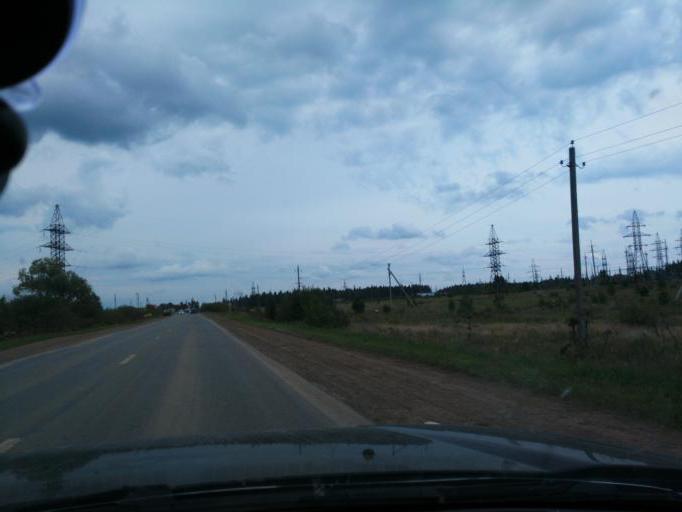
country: RU
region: Perm
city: Chernushka
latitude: 56.5329
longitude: 56.0802
